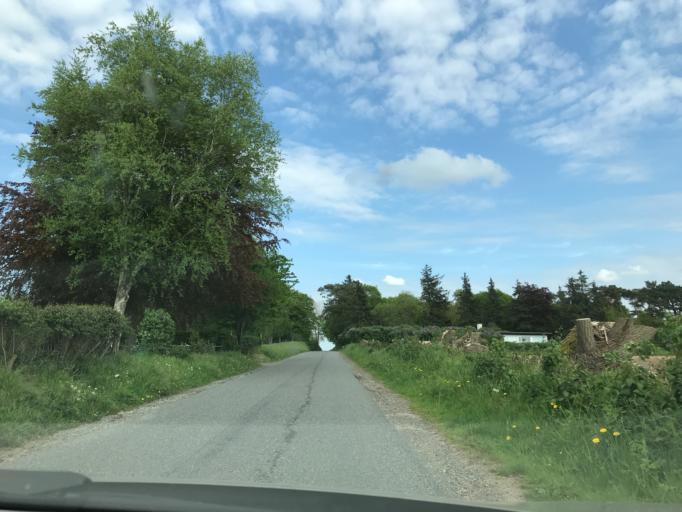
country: DK
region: South Denmark
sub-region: Assens Kommune
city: Assens
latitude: 55.3245
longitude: 9.9115
